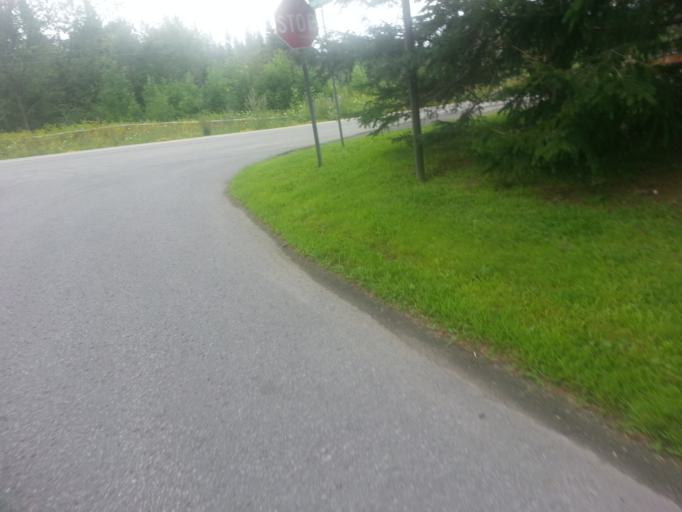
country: CA
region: Ontario
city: Bells Corners
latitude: 45.3273
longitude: -75.9295
